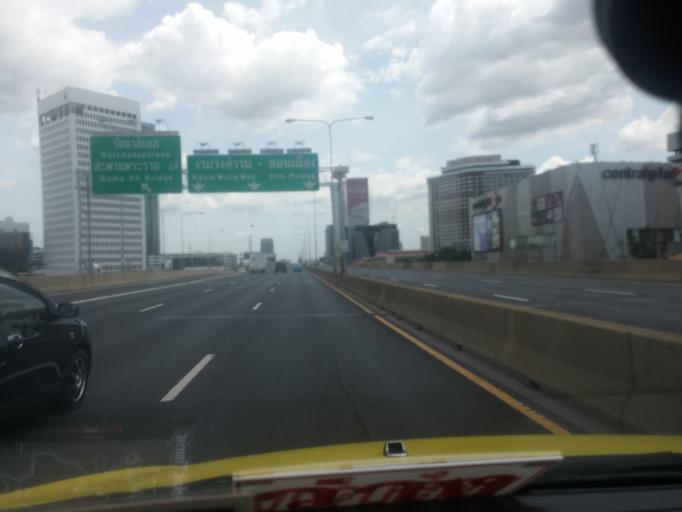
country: TH
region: Bangkok
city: Chatuchak
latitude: 13.8142
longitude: 100.5592
